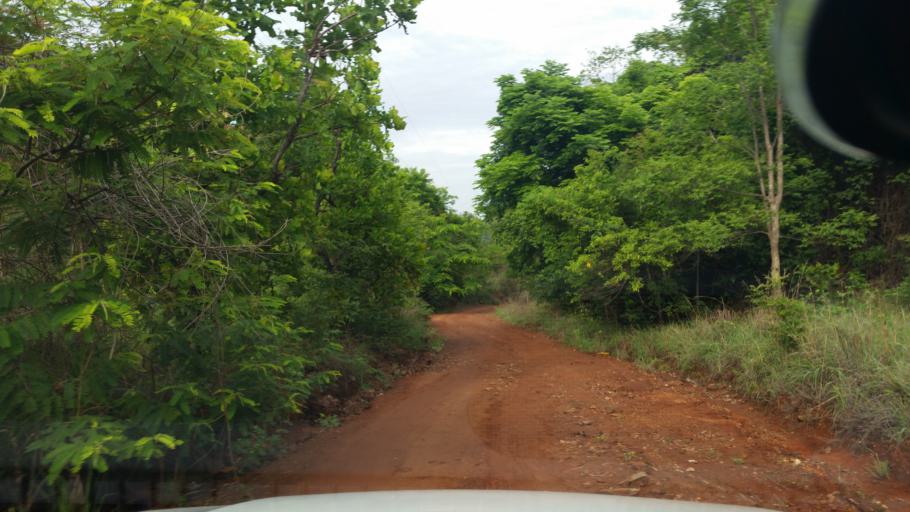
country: BR
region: Goias
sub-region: Porangatu
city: Porangatu
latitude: -13.9803
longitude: -49.2718
